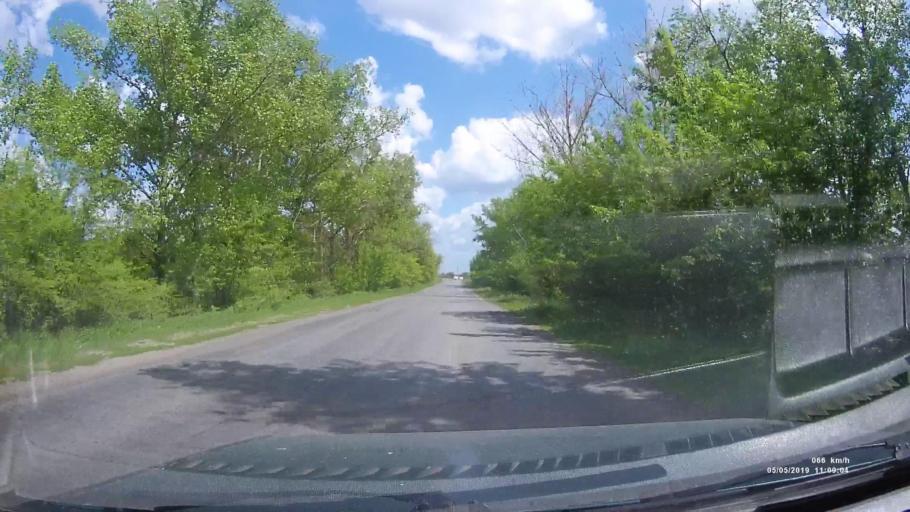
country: RU
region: Rostov
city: Ust'-Donetskiy
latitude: 47.7385
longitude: 40.9207
